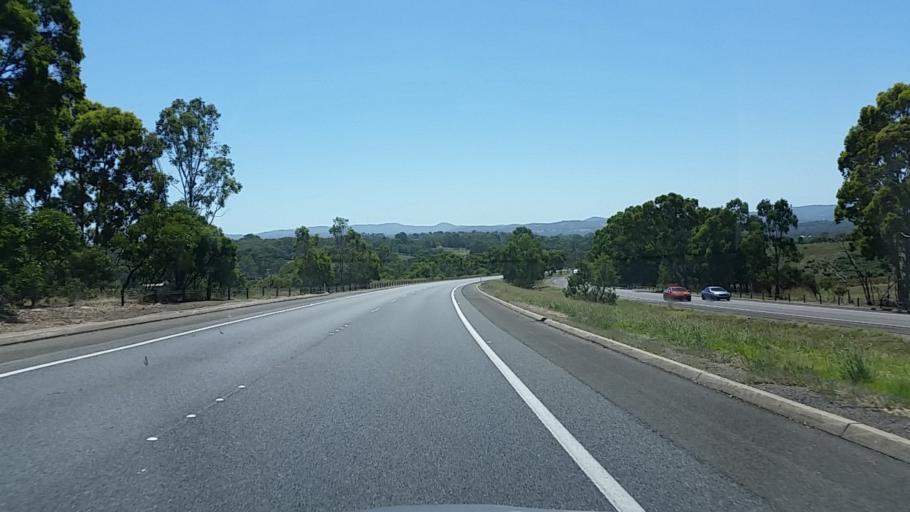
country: AU
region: South Australia
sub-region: Mount Barker
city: Hahndorf
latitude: -35.0468
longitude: 138.8201
